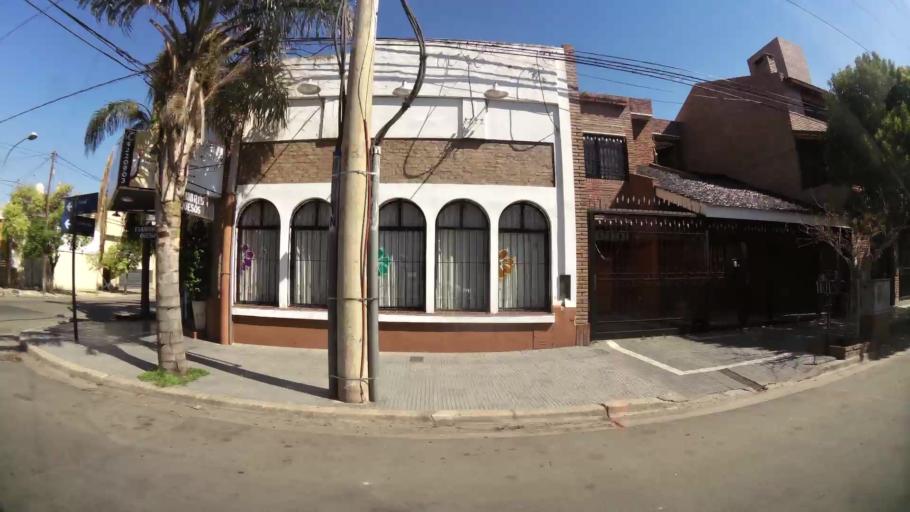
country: AR
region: Cordoba
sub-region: Departamento de Capital
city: Cordoba
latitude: -31.4013
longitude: -64.1706
